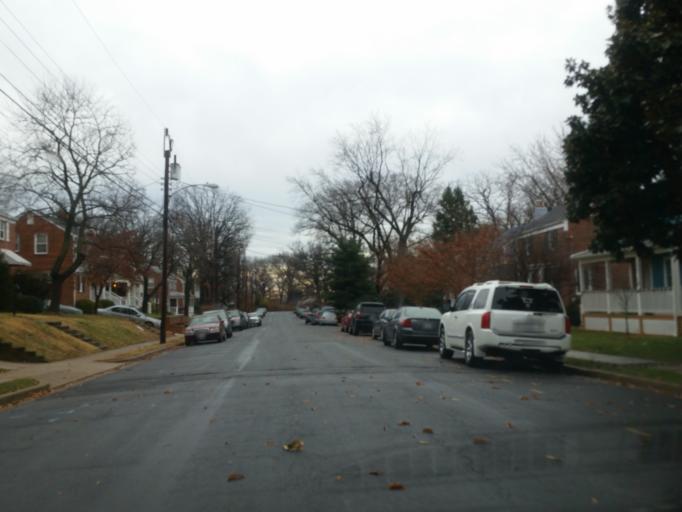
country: US
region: Virginia
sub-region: Arlington County
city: Arlington
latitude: 38.8656
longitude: -77.1116
